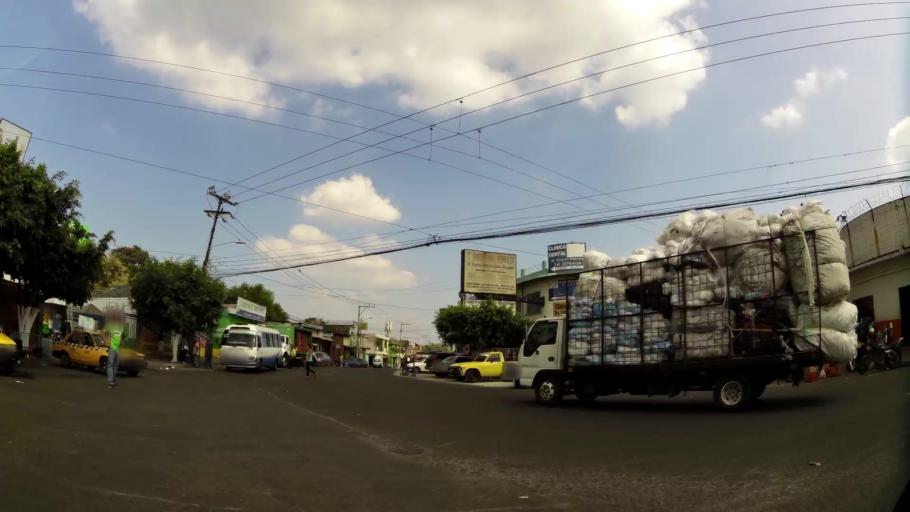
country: SV
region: San Salvador
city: Delgado
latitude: 13.7213
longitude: -89.1691
